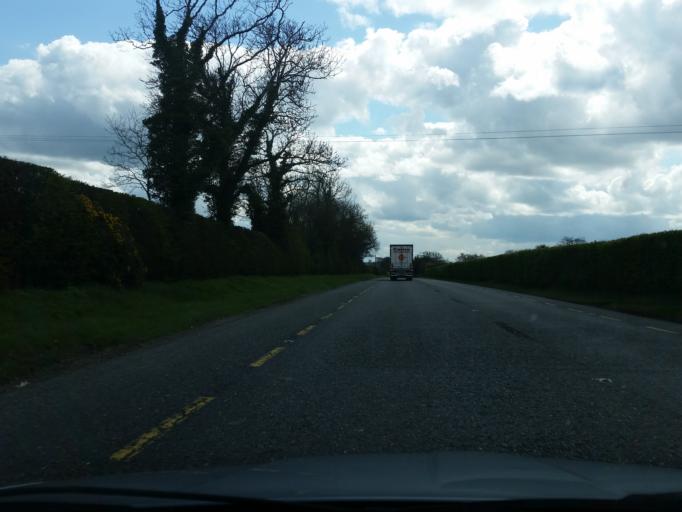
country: IE
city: Kentstown
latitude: 53.6150
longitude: -6.4804
